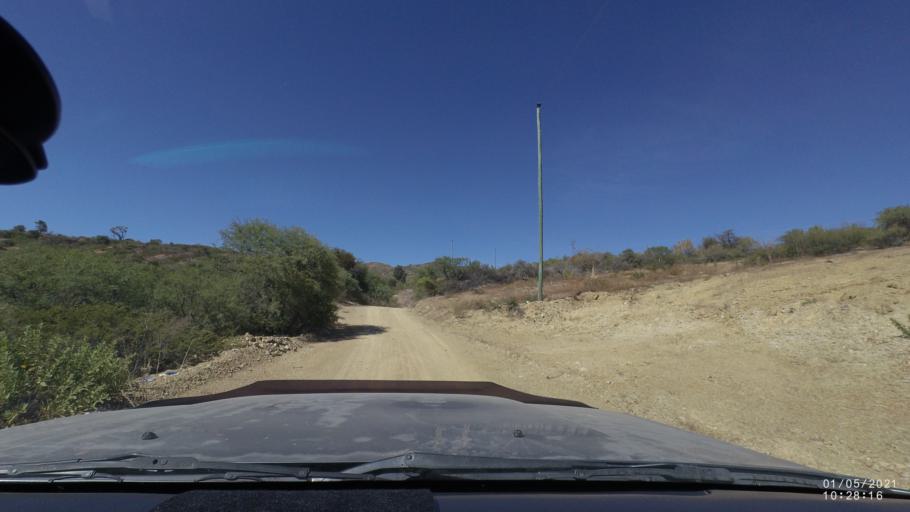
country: BO
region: Cochabamba
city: Capinota
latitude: -17.5886
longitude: -66.1898
